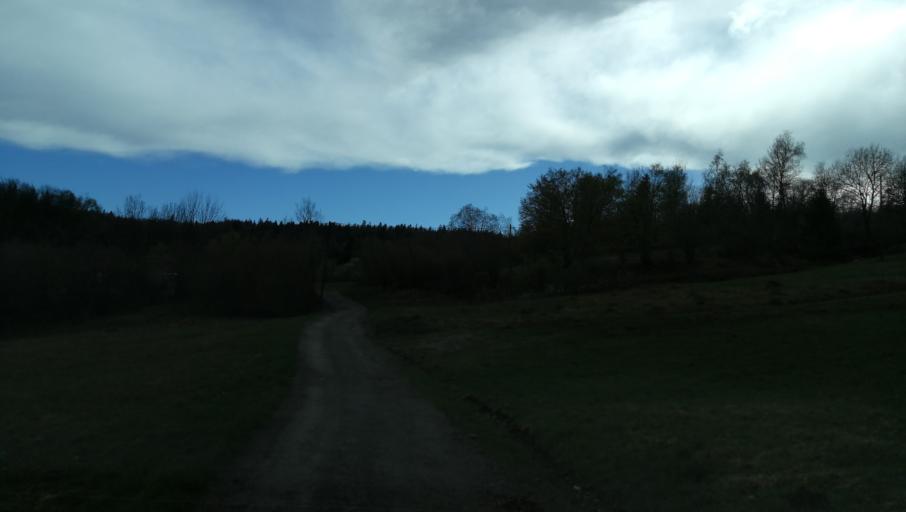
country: FR
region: Franche-Comte
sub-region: Departement du Jura
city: Lavans-les-Saint-Claude
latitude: 46.3154
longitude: 5.8066
